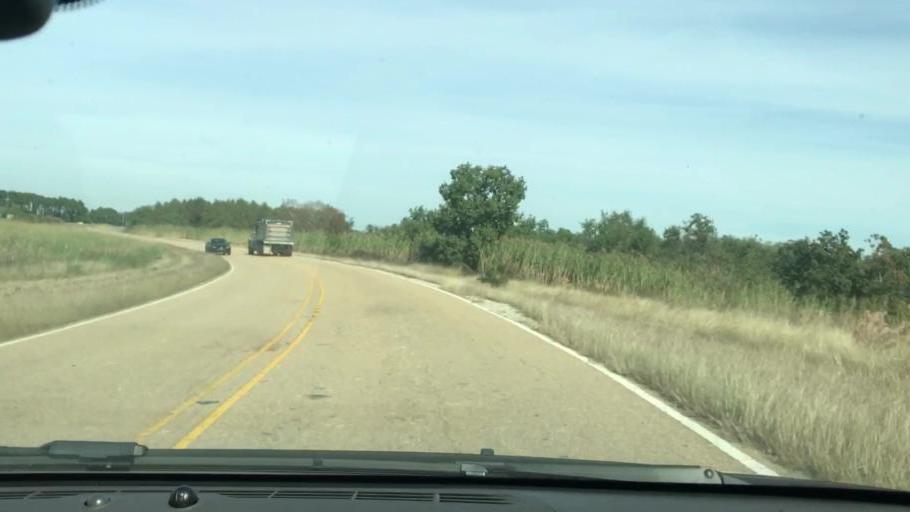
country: US
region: Louisiana
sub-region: Saint Tammany Parish
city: Eden Isle
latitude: 30.2204
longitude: -89.7778
